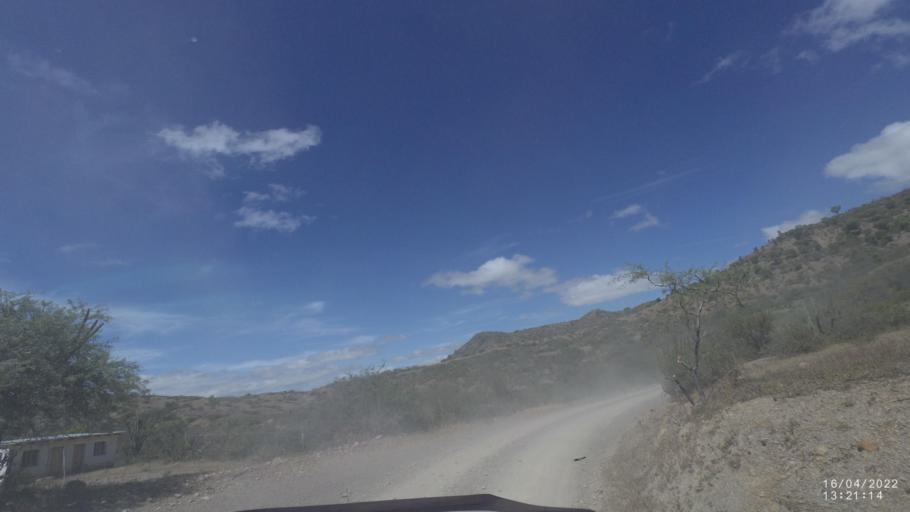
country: BO
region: Cochabamba
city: Mizque
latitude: -17.9912
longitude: -65.6113
